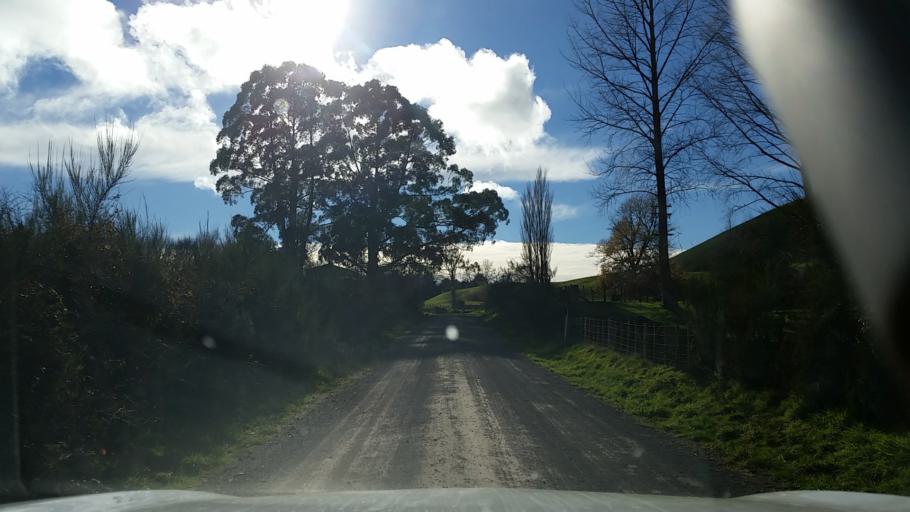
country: NZ
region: Bay of Plenty
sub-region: Rotorua District
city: Rotorua
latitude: -38.3747
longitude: 176.2054
